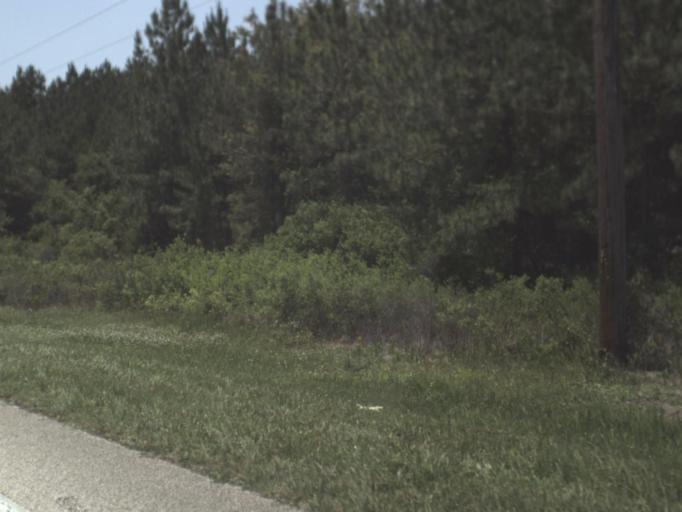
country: US
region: Florida
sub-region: Bradford County
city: Starke
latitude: 30.0967
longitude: -82.0561
